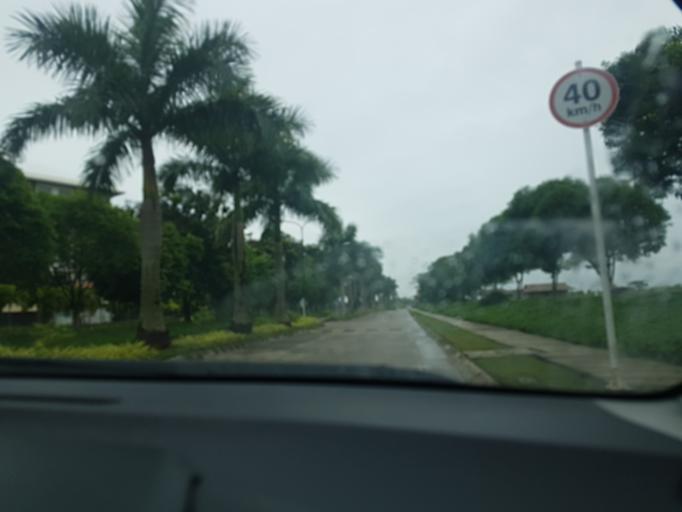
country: MM
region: Yangon
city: Syriam
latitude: 16.7764
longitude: 96.2270
